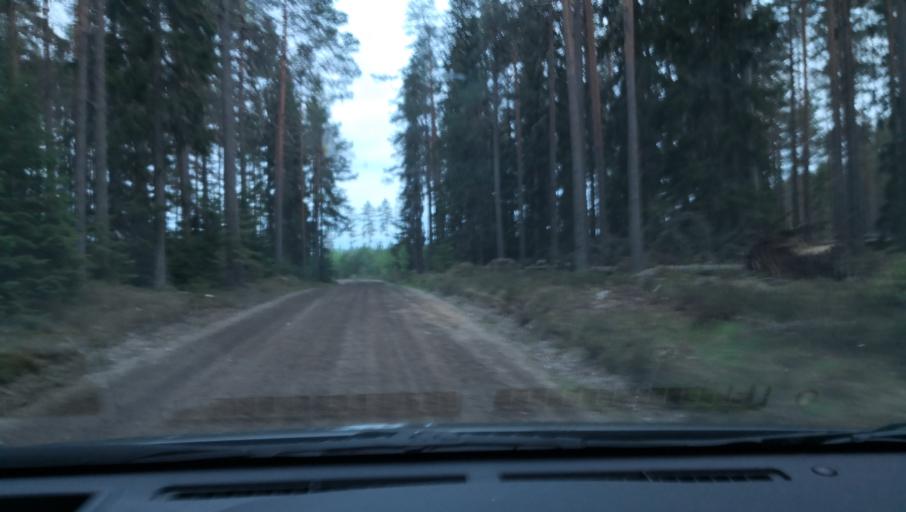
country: SE
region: Vaestmanland
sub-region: Skinnskattebergs Kommun
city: Skinnskatteberg
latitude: 59.7110
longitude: 15.5127
